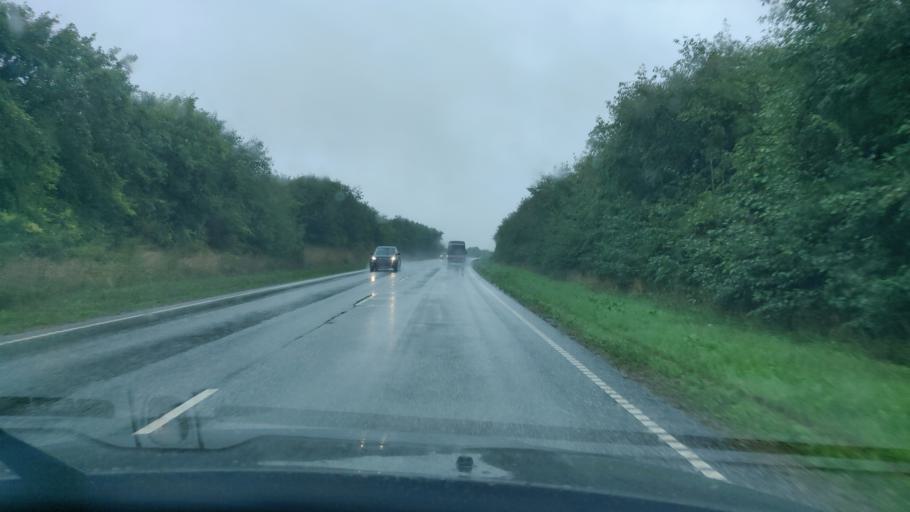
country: DK
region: North Denmark
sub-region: Thisted Kommune
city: Thisted
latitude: 56.9701
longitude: 8.6587
